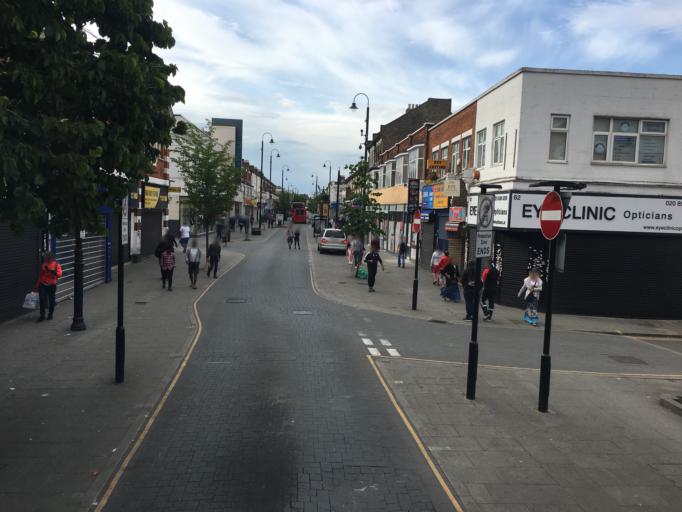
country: GB
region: England
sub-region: Greater London
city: East Ham
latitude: 51.5347
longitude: 0.0532
